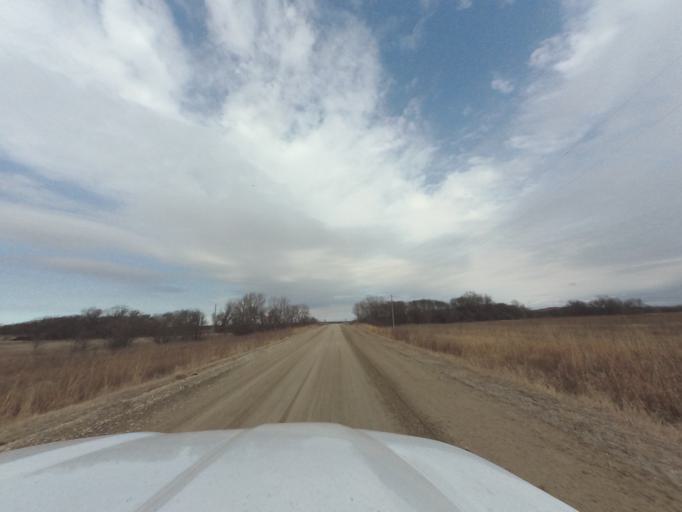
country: US
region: Kansas
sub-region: Chase County
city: Cottonwood Falls
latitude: 38.2929
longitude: -96.7321
